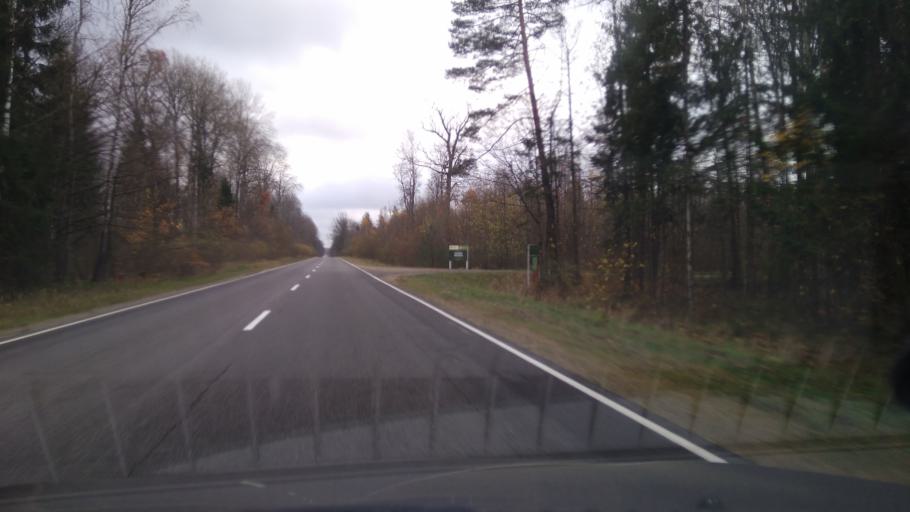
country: BY
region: Minsk
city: Urechcha
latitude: 53.2116
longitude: 27.8856
